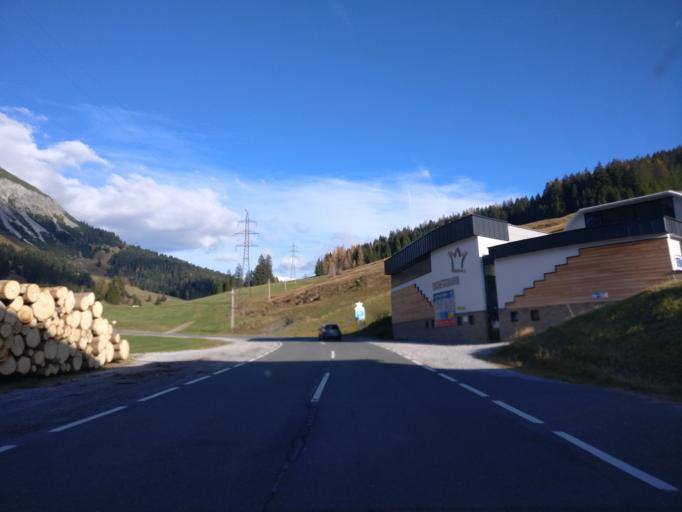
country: AT
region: Salzburg
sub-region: Politischer Bezirk Zell am See
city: Dienten am Hochkonig
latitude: 47.3891
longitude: 13.0334
